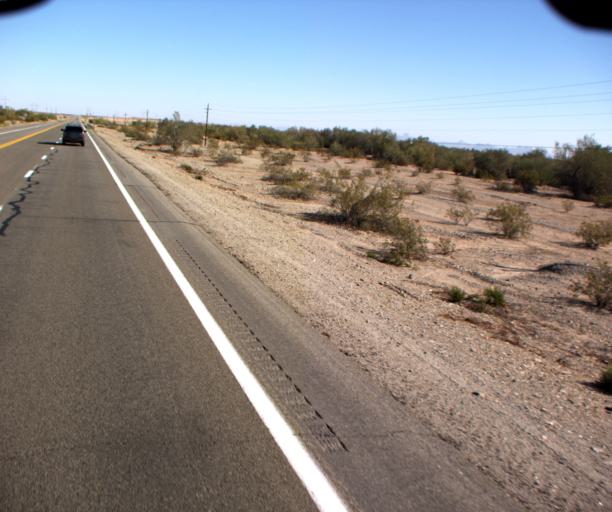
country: US
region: Arizona
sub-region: Yuma County
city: Fortuna Foothills
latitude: 32.7950
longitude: -114.3813
